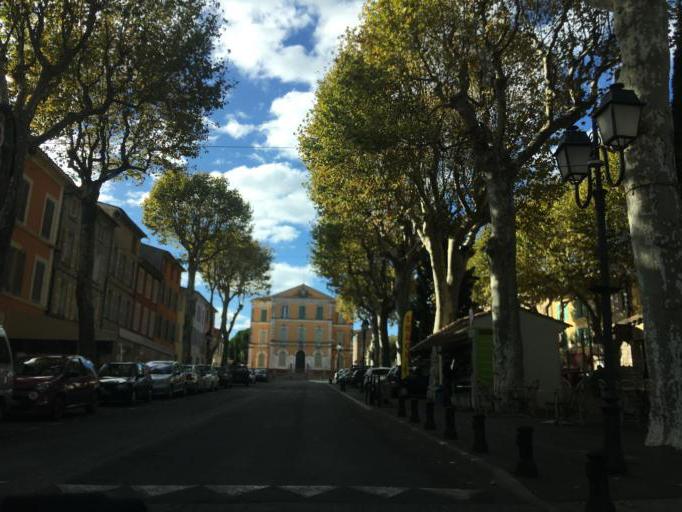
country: FR
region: Provence-Alpes-Cote d'Azur
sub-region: Departement du Var
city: Lorgues
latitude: 43.4932
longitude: 6.3581
